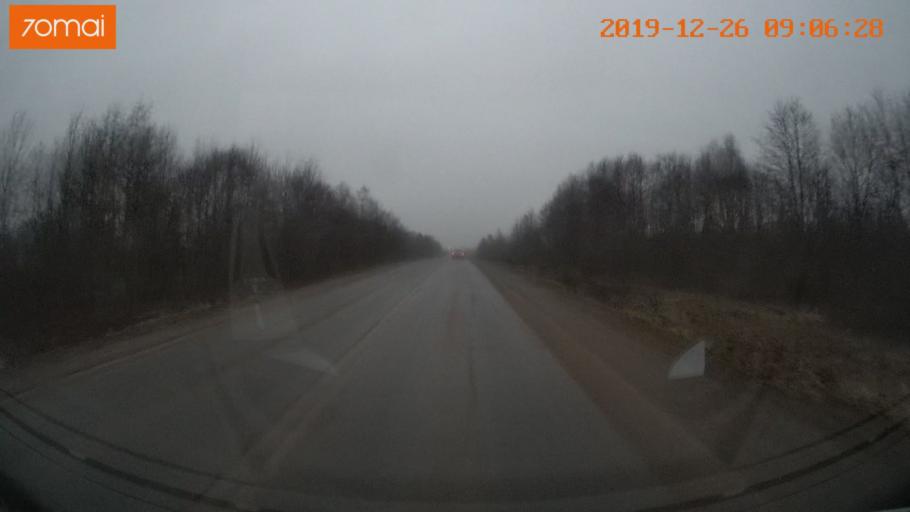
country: RU
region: Vologda
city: Gryazovets
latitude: 58.8367
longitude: 40.2536
